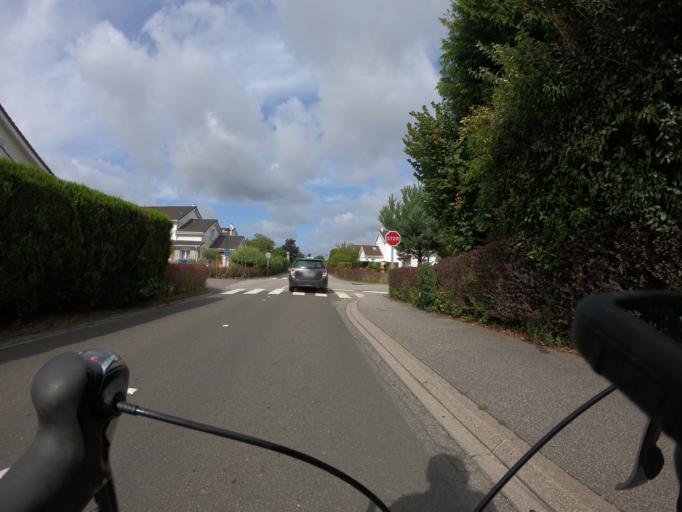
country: FR
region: Ile-de-France
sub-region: Departement des Yvelines
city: Voisins-le-Bretonneux
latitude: 48.7546
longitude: 2.0524
